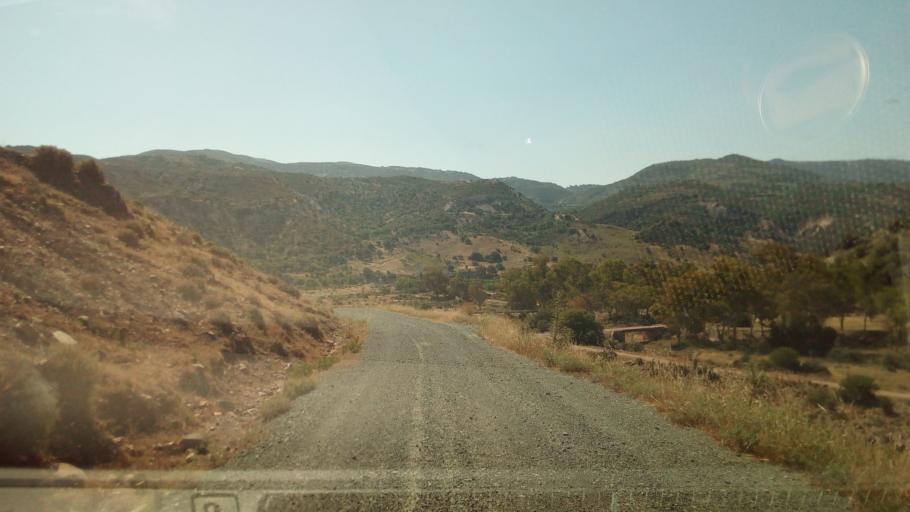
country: CY
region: Limassol
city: Pachna
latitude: 34.8111
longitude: 32.7105
